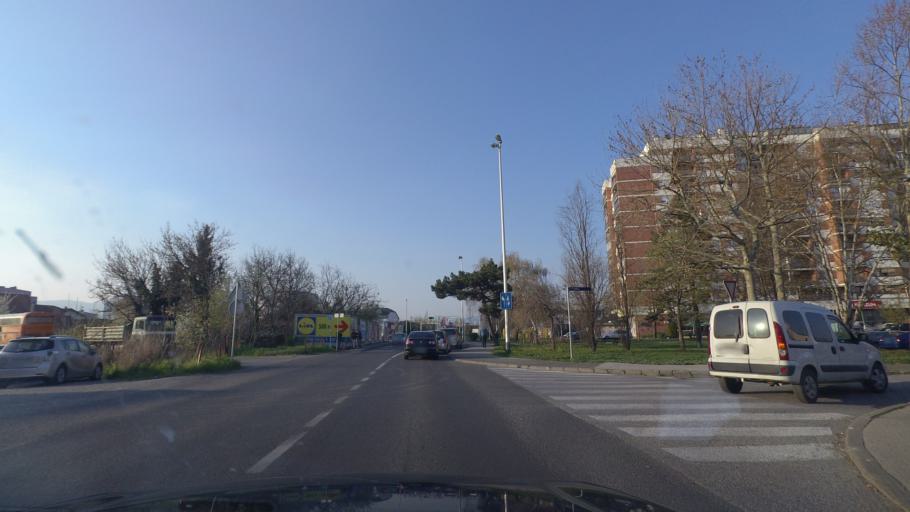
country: HR
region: Grad Zagreb
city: Dubrava
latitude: 45.8278
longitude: 16.0631
